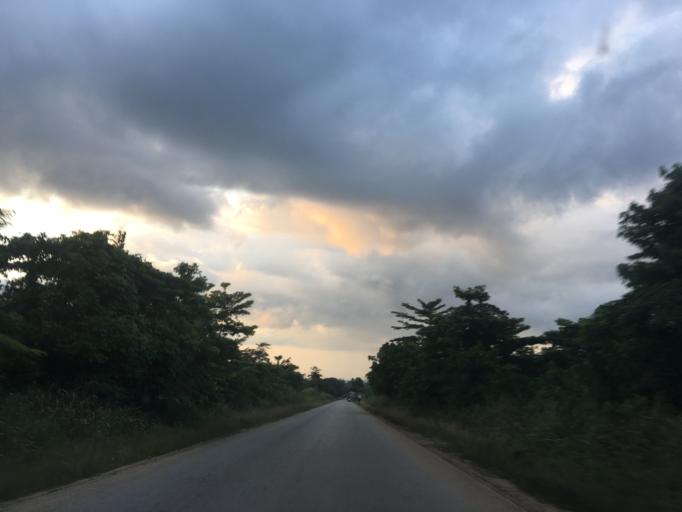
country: GH
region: Western
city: Bibiani
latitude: 6.7432
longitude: -2.5037
